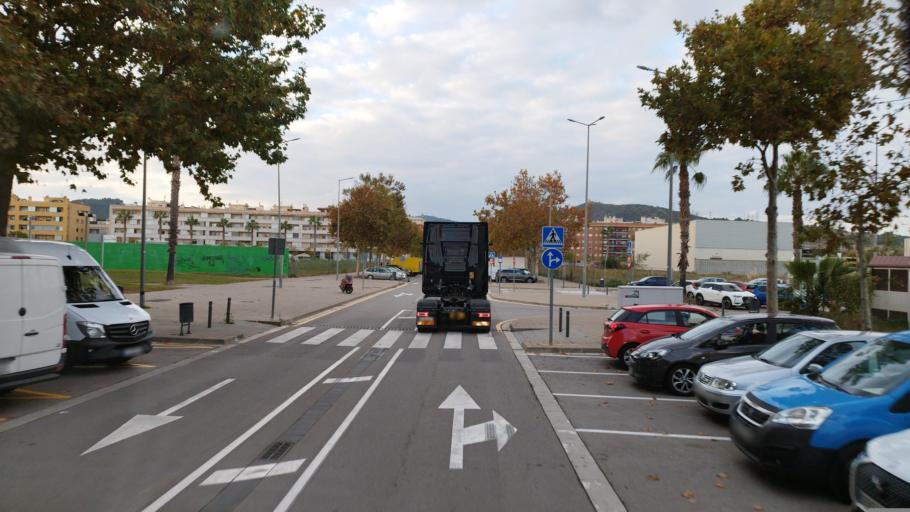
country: ES
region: Catalonia
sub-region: Provincia de Barcelona
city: Viladecans
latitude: 41.3154
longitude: 2.0313
